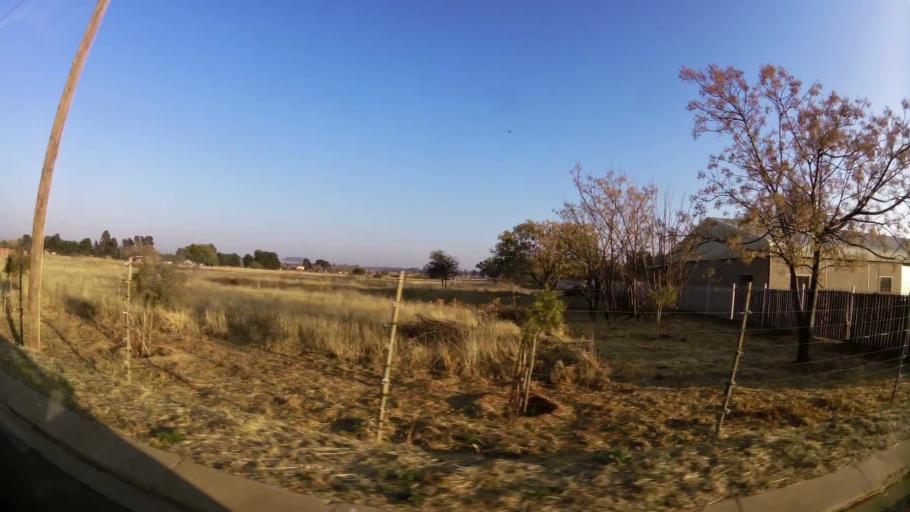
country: ZA
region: Orange Free State
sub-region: Mangaung Metropolitan Municipality
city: Bloemfontein
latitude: -29.0851
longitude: 26.1447
